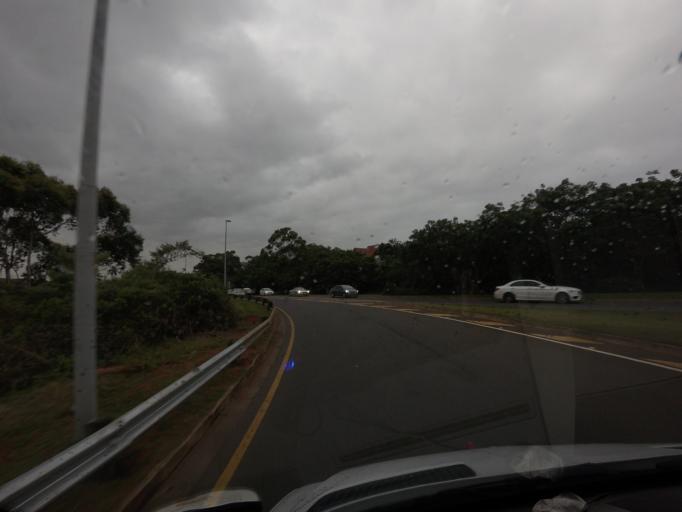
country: ZA
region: KwaZulu-Natal
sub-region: iLembe District Municipality
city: Ballitoville
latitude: -29.5382
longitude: 31.1956
